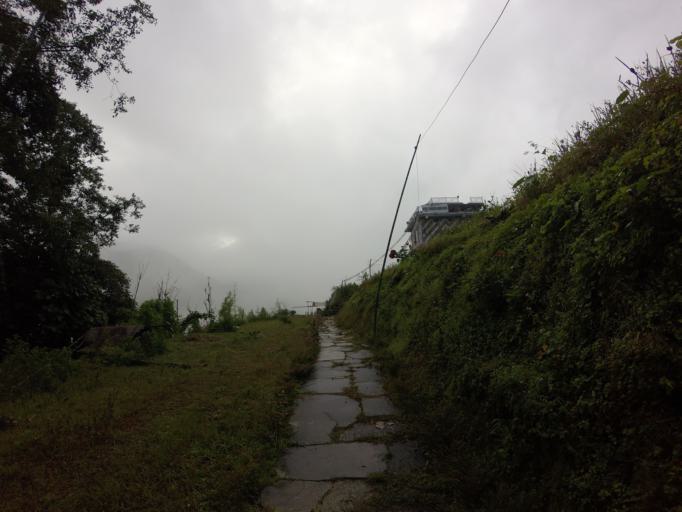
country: NP
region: Western Region
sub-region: Gandaki Zone
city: Pokhara
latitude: 28.3836
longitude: 83.8738
